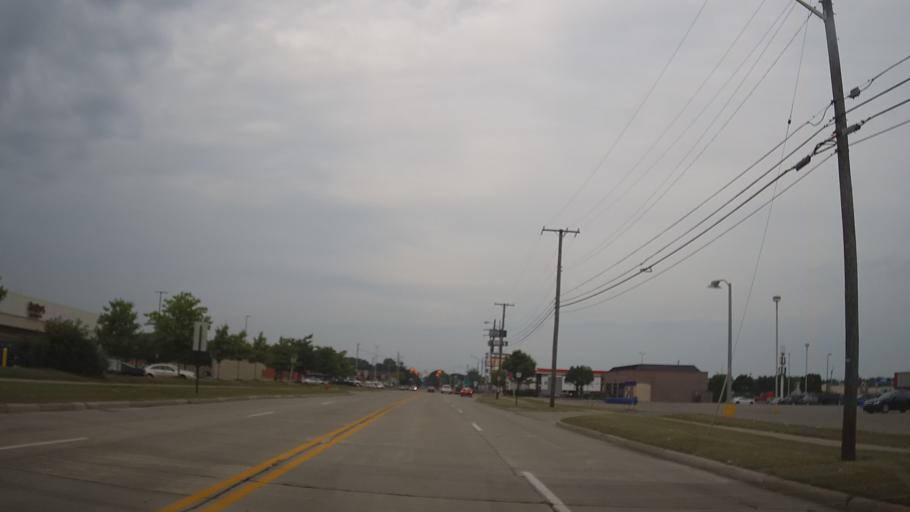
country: US
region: Michigan
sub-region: Macomb County
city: Fraser
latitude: 42.5324
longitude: -82.9109
